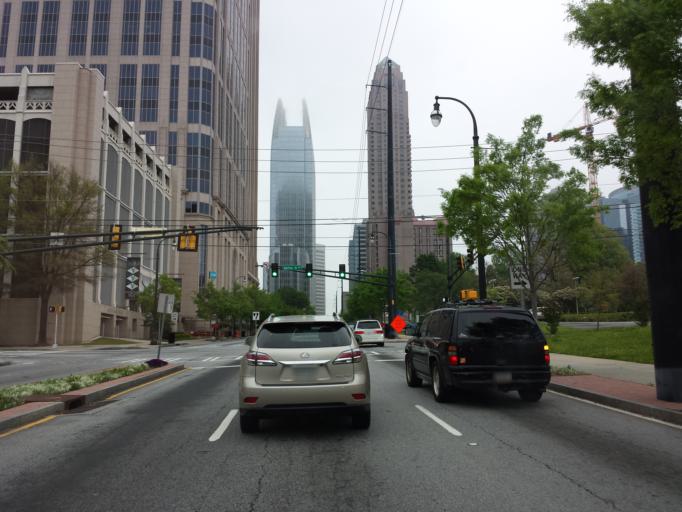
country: US
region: Georgia
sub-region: Fulton County
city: Atlanta
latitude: 33.7866
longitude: -84.3897
